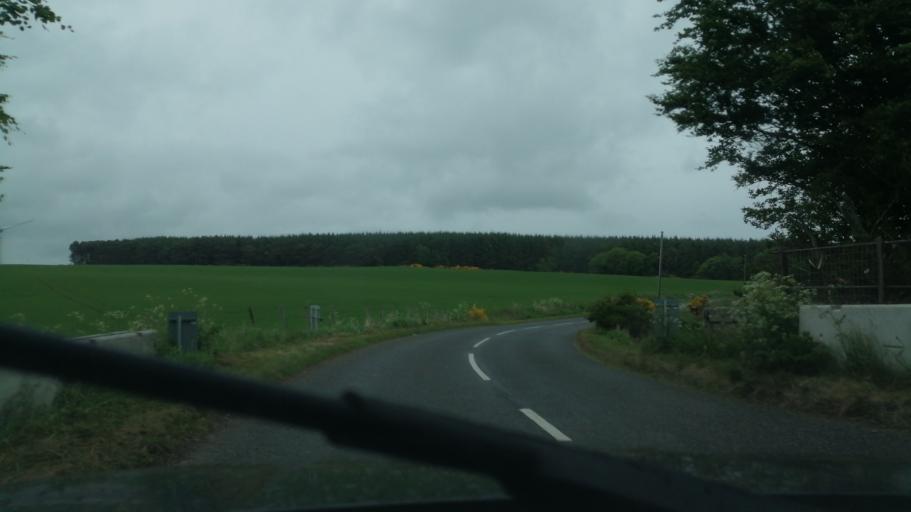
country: GB
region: Scotland
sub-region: Aberdeenshire
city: Portsoy
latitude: 57.6007
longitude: -2.7292
